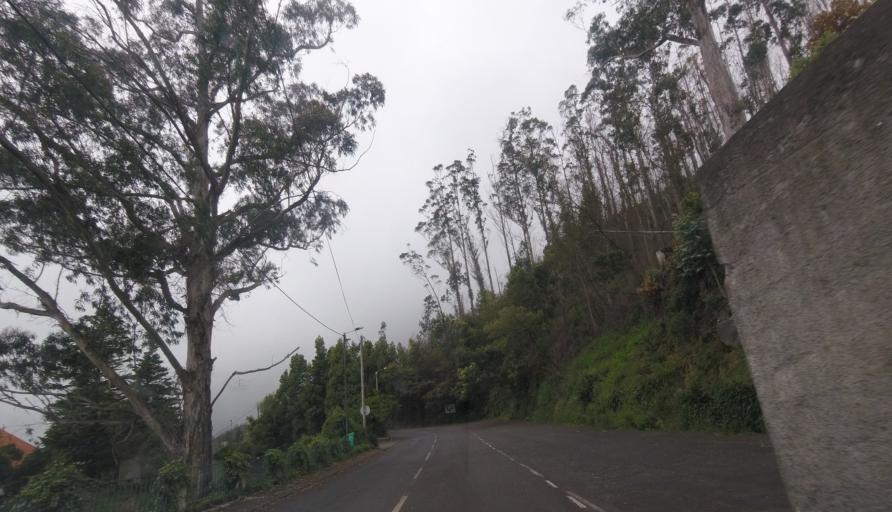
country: PT
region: Madeira
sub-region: Funchal
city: Nossa Senhora do Monte
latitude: 32.6848
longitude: -16.9000
